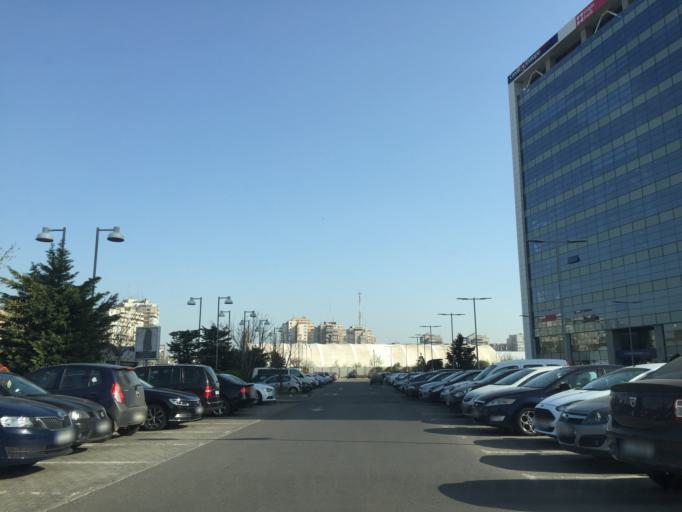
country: RO
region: Ilfov
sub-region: Comuna Chiajna
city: Rosu
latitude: 44.4296
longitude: 26.0349
